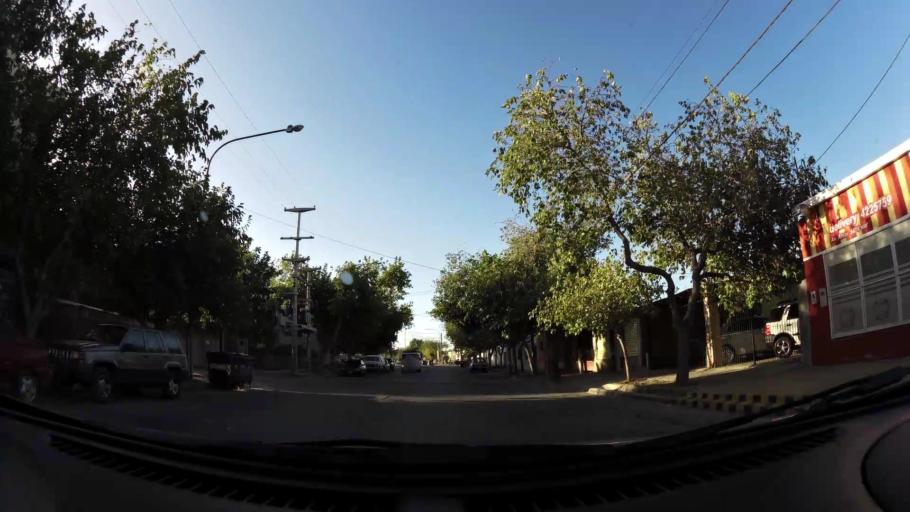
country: AR
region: San Juan
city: Villa Krause
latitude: -31.5521
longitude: -68.5261
